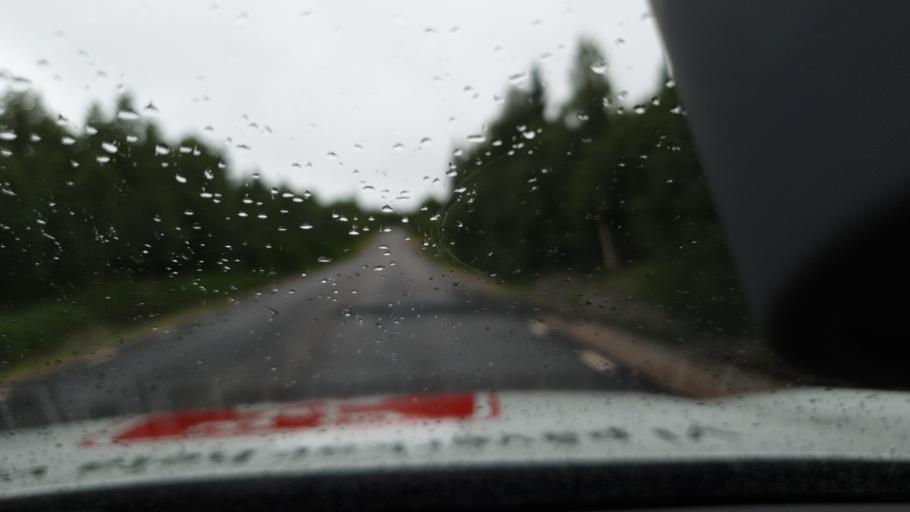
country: SE
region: Norrbotten
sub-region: Overtornea Kommun
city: OEvertornea
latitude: 66.4889
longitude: 23.4523
